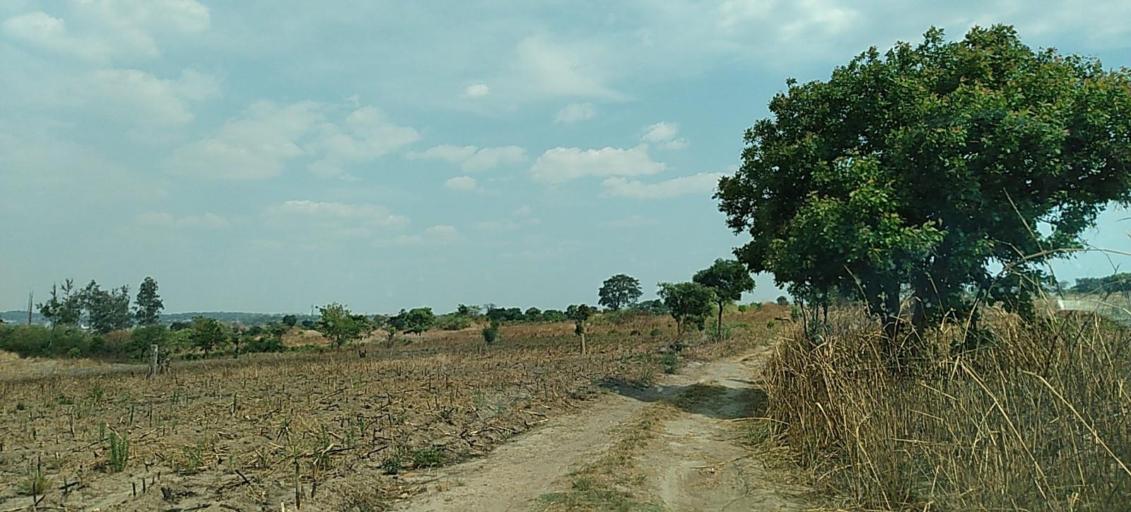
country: ZM
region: Copperbelt
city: Chililabombwe
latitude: -12.3480
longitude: 27.7931
